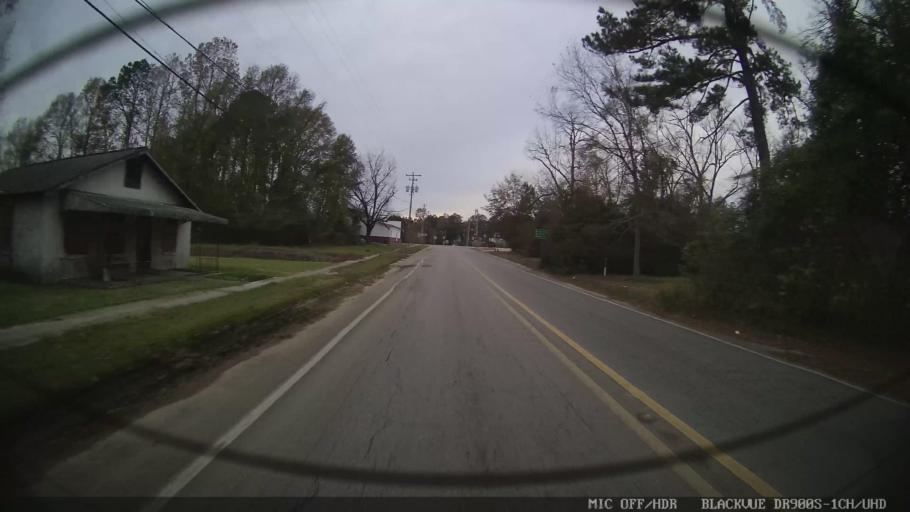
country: US
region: Mississippi
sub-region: Clarke County
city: Stonewall
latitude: 32.0398
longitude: -88.8833
